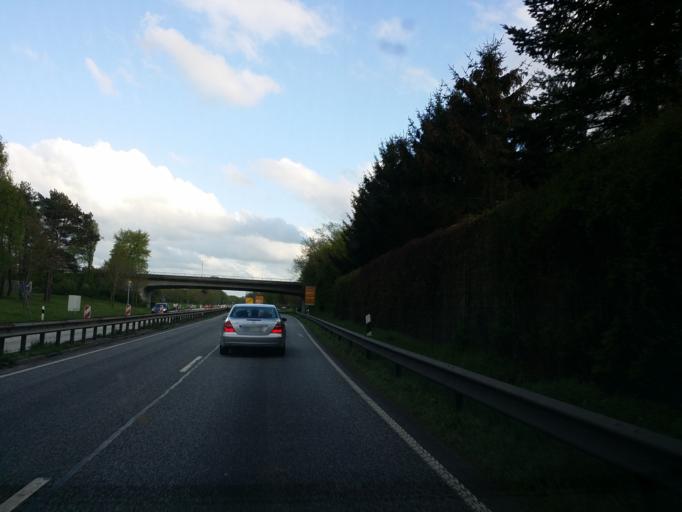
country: DE
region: Schleswig-Holstein
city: Westerronfeld
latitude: 54.2798
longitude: 9.6594
